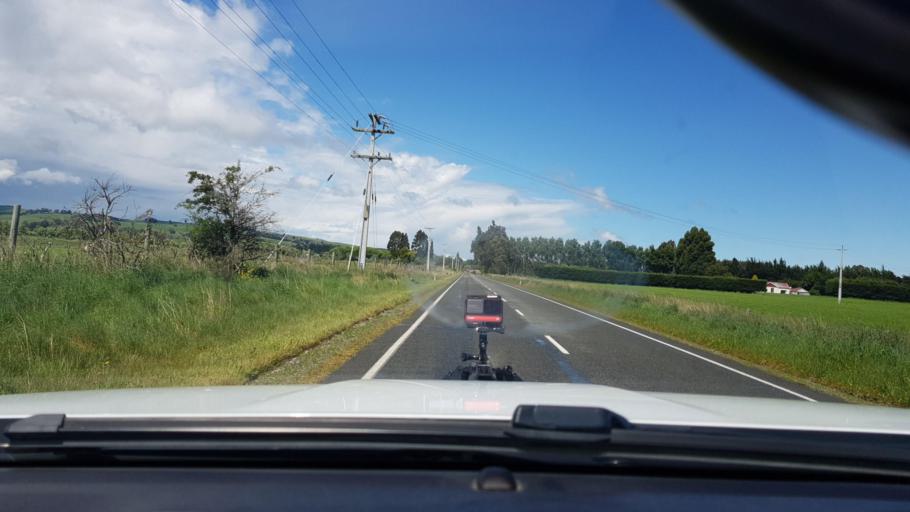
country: NZ
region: Southland
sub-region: Southland District
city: Winton
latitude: -45.8789
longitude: 168.3584
